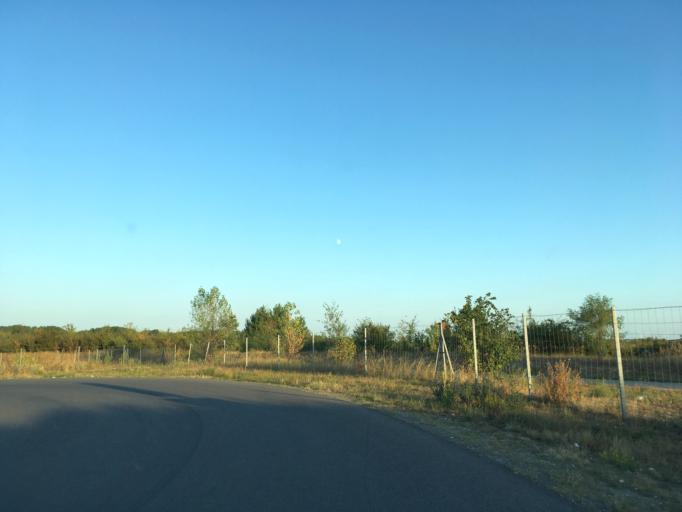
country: AT
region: Burgenland
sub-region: Politischer Bezirk Neusiedl am See
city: Potzneusiedl
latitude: 48.0315
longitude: 16.9602
